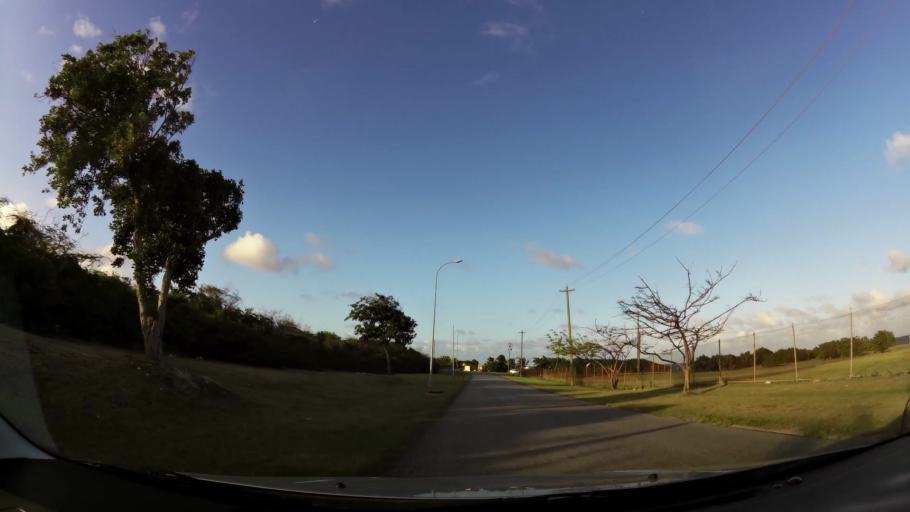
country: AG
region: Saint George
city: Piggotts
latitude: 17.1602
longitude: -61.7981
